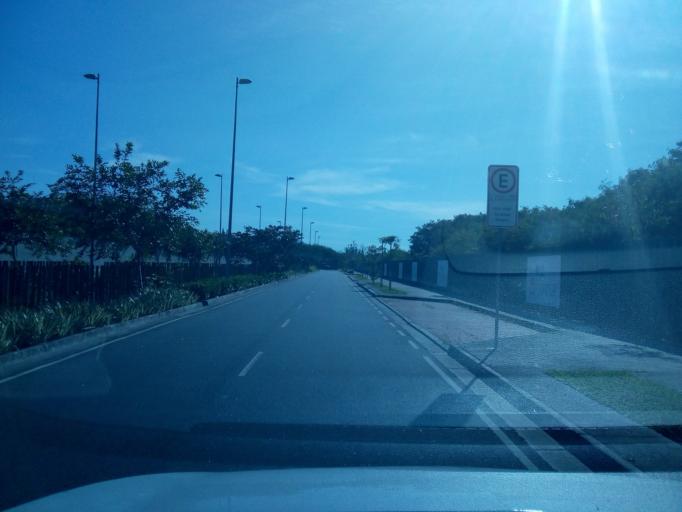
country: BR
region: Rio de Janeiro
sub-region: Nilopolis
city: Nilopolis
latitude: -23.0218
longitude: -43.5079
